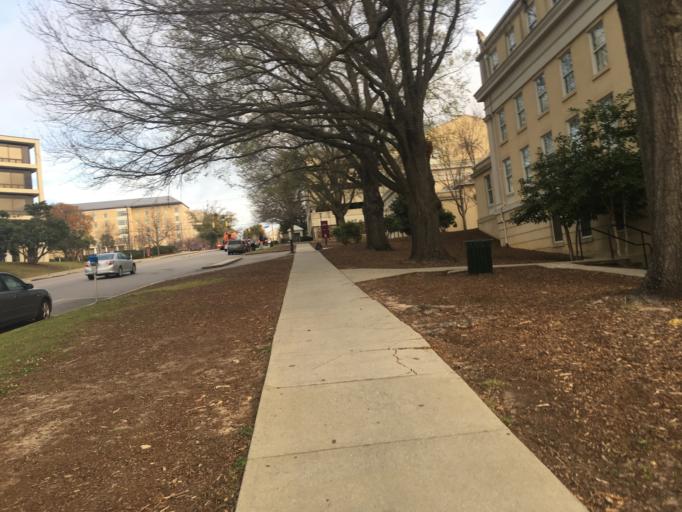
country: US
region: South Carolina
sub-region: Richland County
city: Columbia
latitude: 33.9925
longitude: -81.0277
